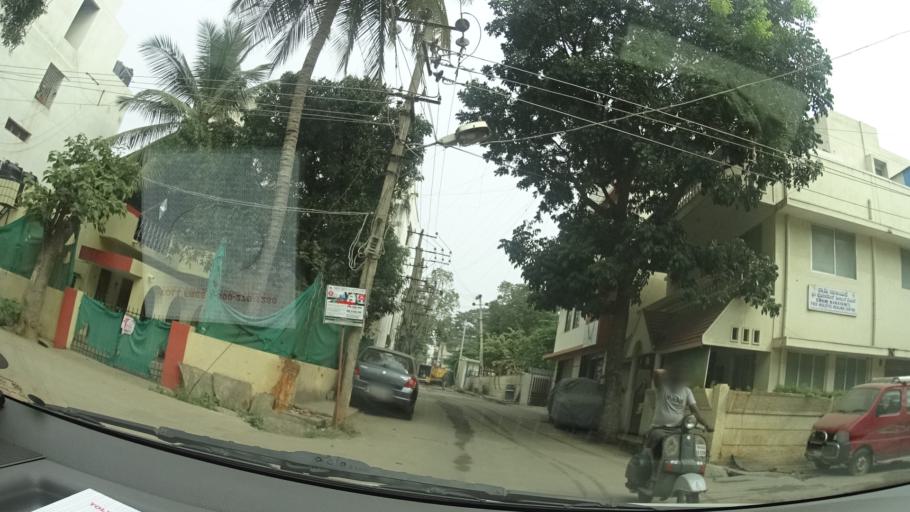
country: IN
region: Karnataka
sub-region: Bangalore Urban
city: Bangalore
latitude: 13.0262
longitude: 77.6300
